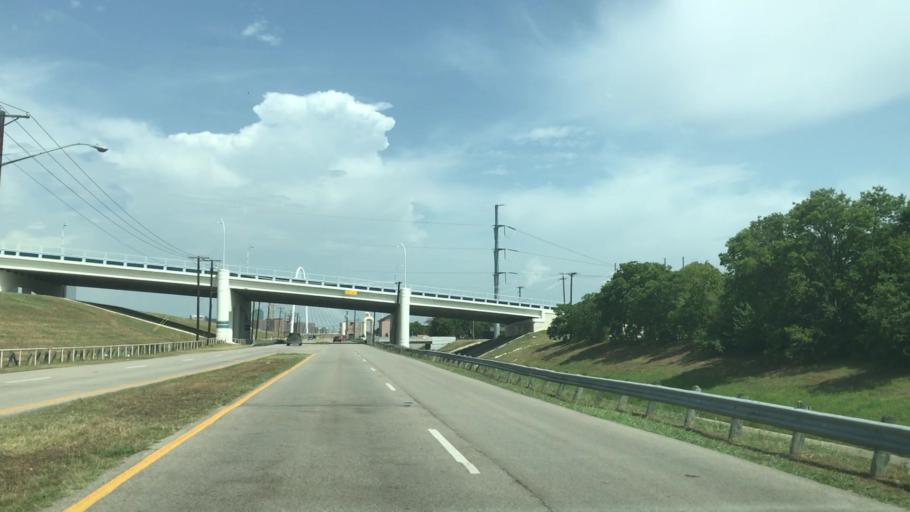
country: US
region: Texas
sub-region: Dallas County
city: Dallas
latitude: 32.7866
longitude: -96.8374
